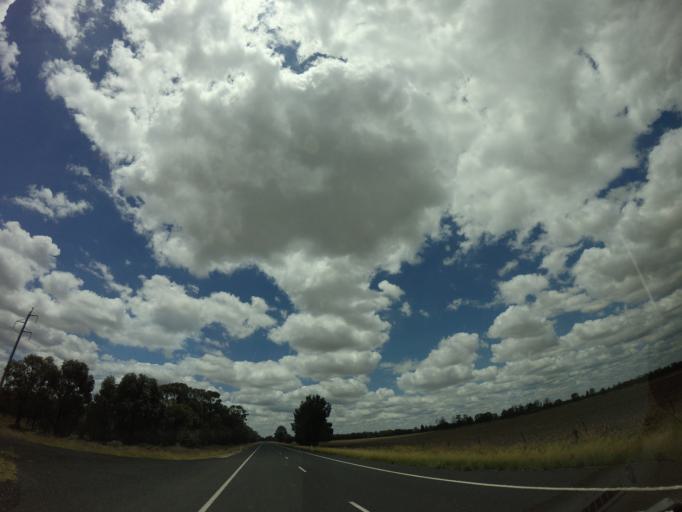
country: AU
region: Queensland
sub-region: Goondiwindi
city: Goondiwindi
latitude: -28.1297
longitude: 150.7007
